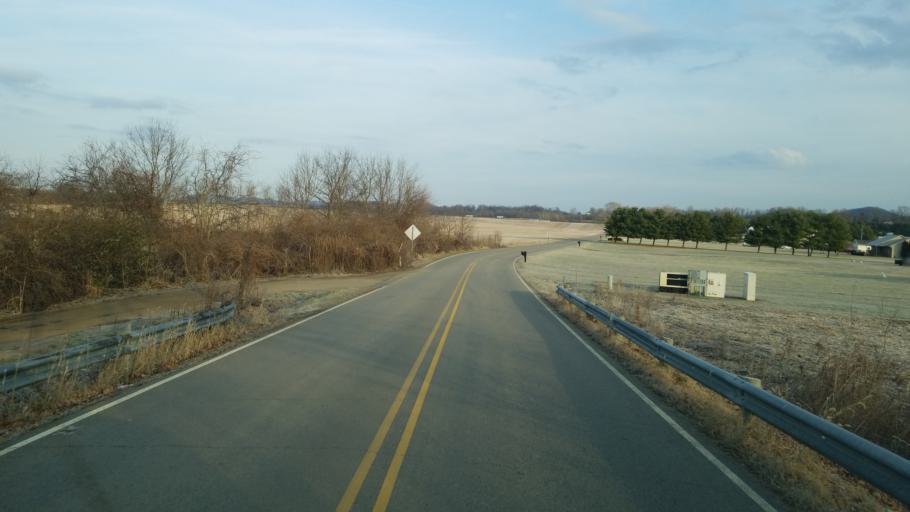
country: US
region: Ohio
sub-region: Ross County
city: Chillicothe
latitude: 39.2525
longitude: -82.8707
